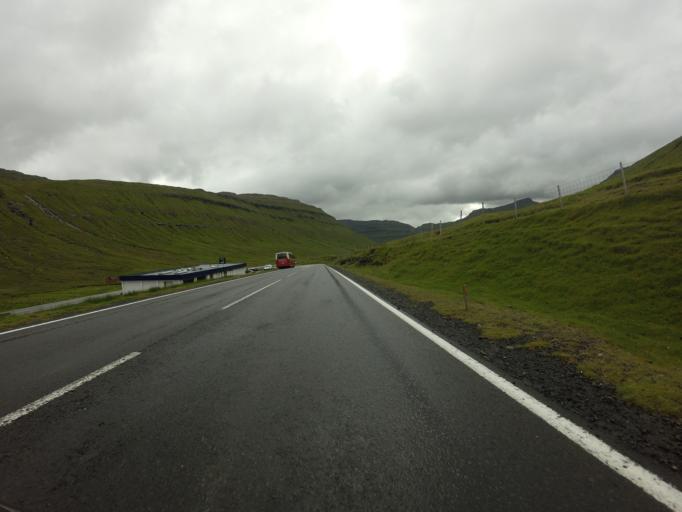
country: FO
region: Streymoy
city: Kollafjordhur
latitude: 62.1193
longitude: -6.9852
